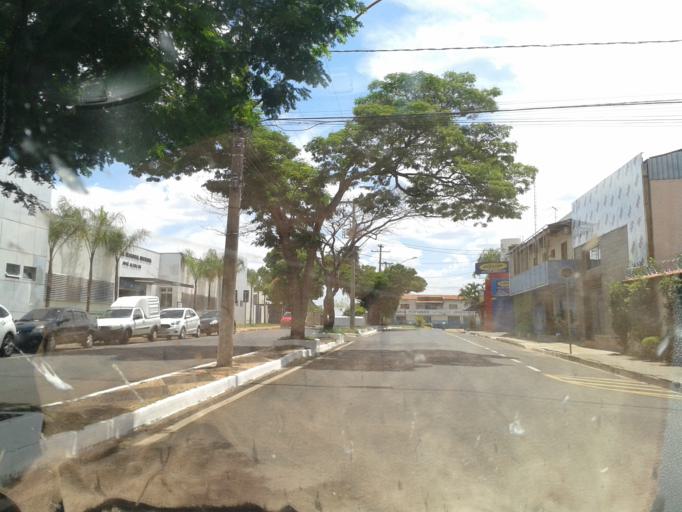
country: BR
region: Minas Gerais
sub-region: Uberaba
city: Uberaba
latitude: -19.7411
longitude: -47.9585
